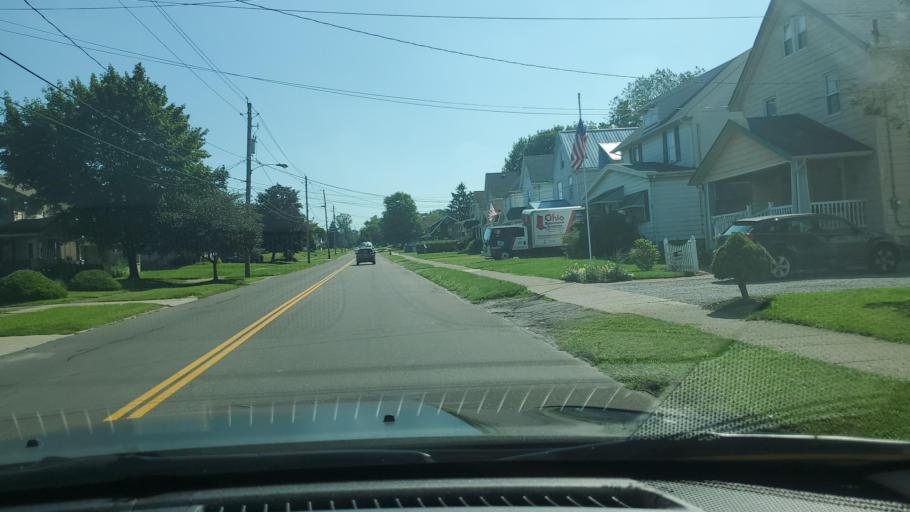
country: US
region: Ohio
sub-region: Trumbull County
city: Girard
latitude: 41.1619
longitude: -80.7008
